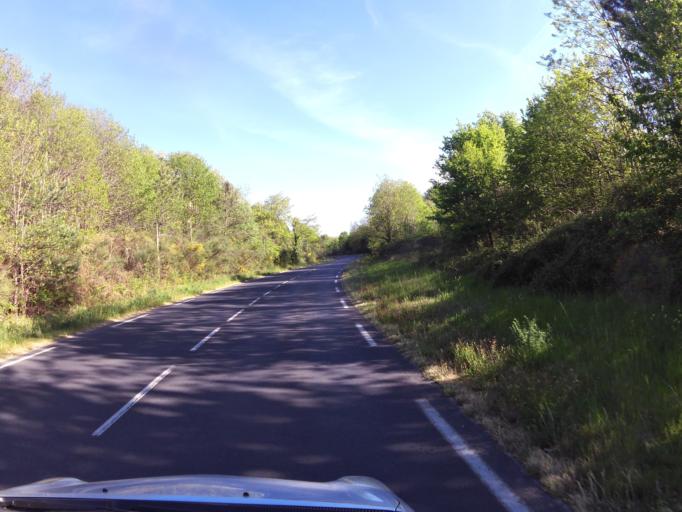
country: FR
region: Aquitaine
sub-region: Departement de la Dordogne
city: Montignac
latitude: 45.0087
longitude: 1.2407
